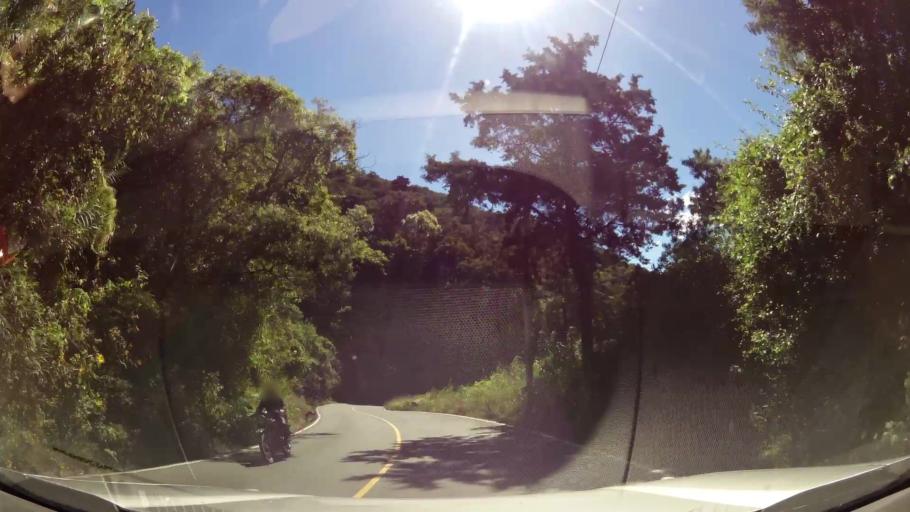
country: GT
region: Solola
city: Panajachel
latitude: 14.7541
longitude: -91.1617
